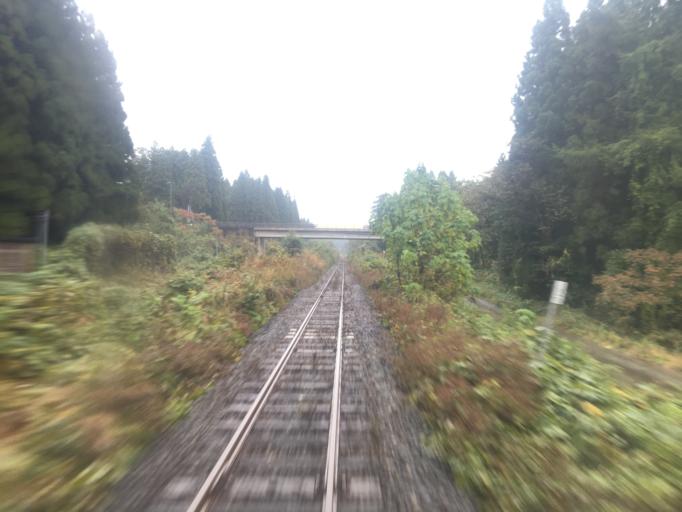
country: JP
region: Yamagata
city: Shinjo
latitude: 38.7049
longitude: 140.3359
